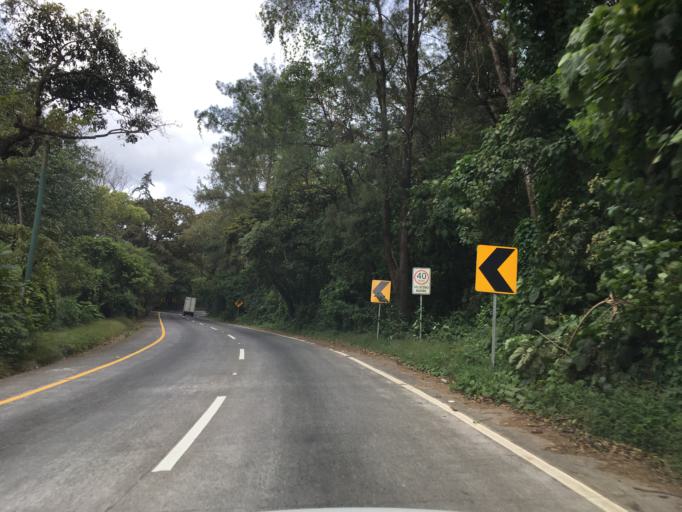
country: GT
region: Sacatepequez
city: Santa Lucia Milpas Altas
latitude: 14.5652
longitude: -90.6892
